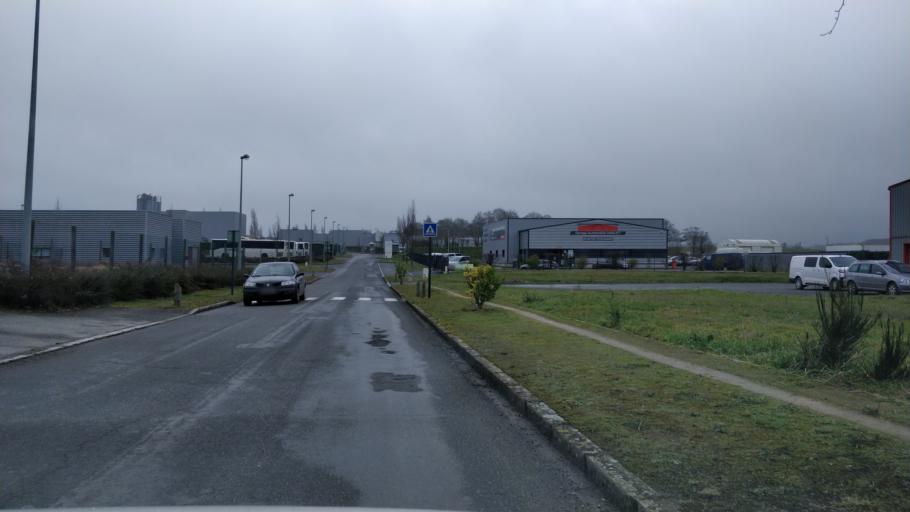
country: FR
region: Brittany
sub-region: Departement des Cotes-d'Armor
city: Broons
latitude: 48.3144
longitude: -2.2465
